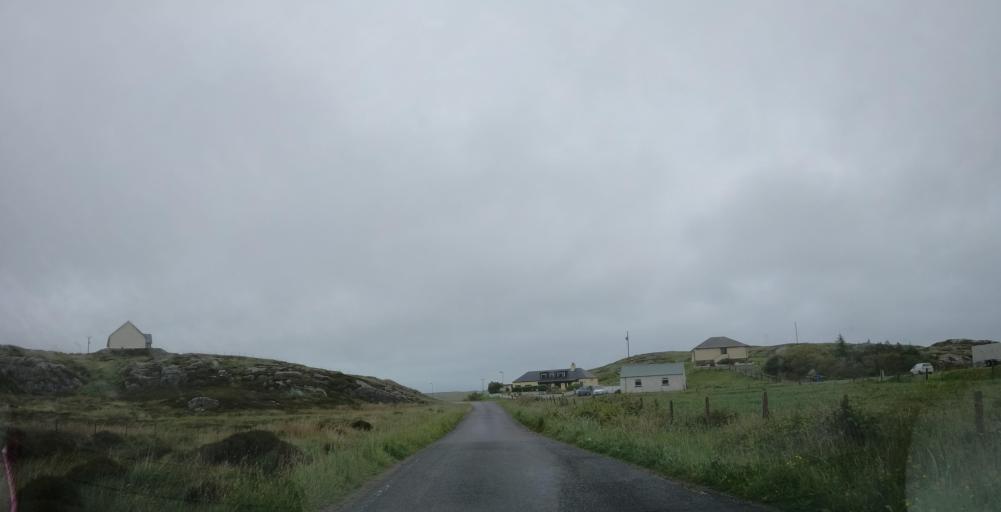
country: GB
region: Scotland
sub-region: Eilean Siar
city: Barra
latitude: 56.9957
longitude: -7.4192
